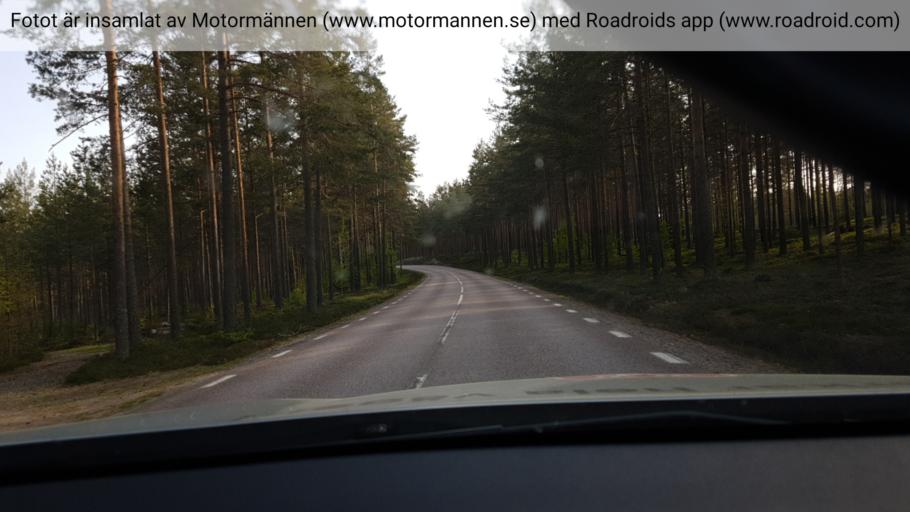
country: SE
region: Gaevleborg
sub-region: Sandvikens Kommun
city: Arsunda
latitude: 60.4671
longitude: 16.7042
